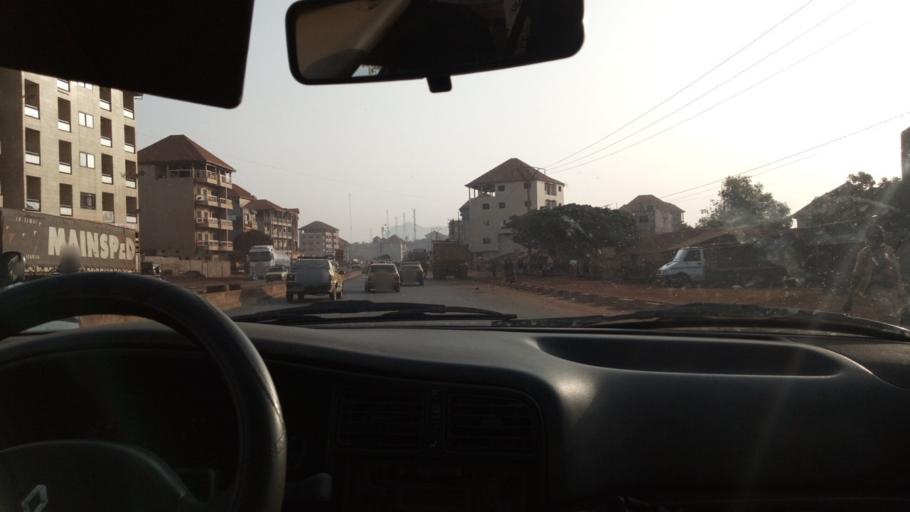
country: GN
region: Kindia
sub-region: Prefecture de Dubreka
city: Dubreka
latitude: 9.6754
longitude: -13.5452
